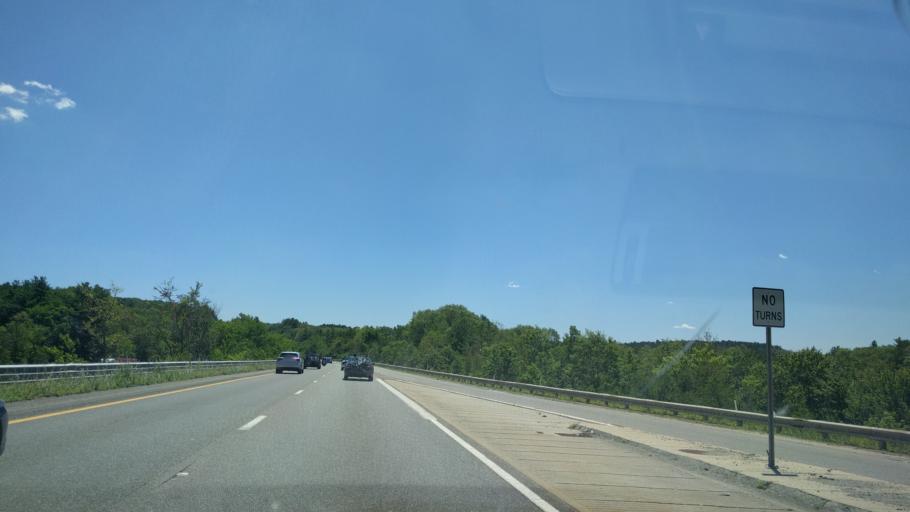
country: US
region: Massachusetts
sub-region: Worcester County
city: East Douglas
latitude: 42.0863
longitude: -71.6932
